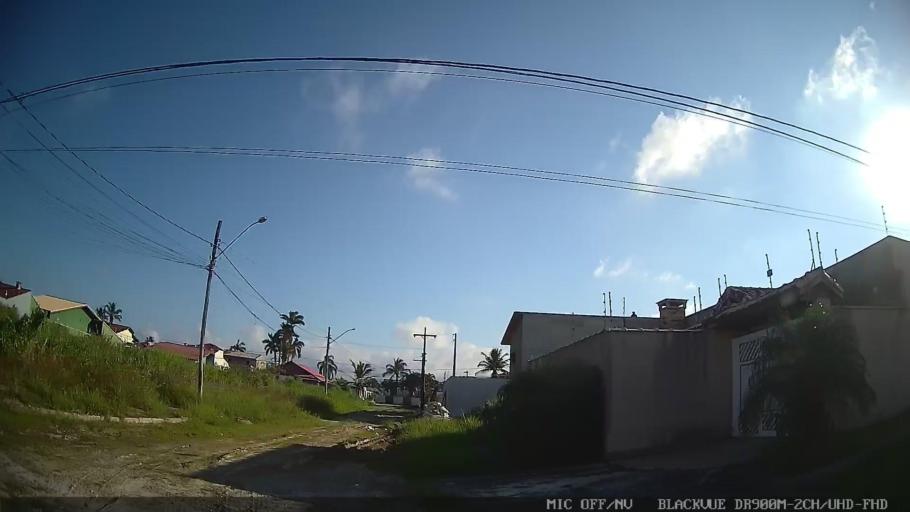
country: BR
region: Sao Paulo
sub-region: Peruibe
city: Peruibe
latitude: -24.2847
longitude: -46.9617
